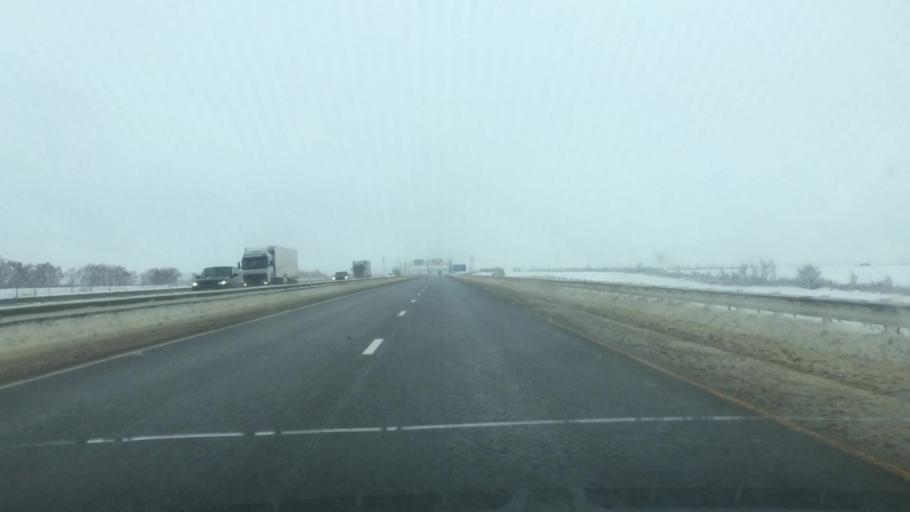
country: RU
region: Tula
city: Yefremov
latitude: 53.2181
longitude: 38.2141
